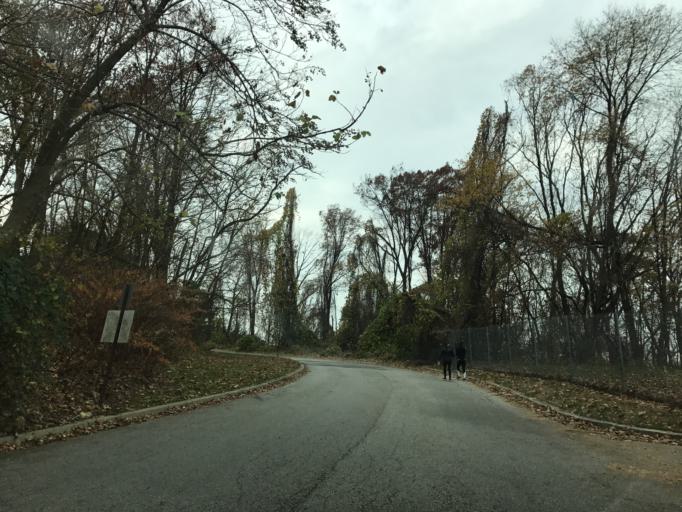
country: US
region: Maryland
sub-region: Baltimore County
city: Hampton
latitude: 39.3995
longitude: -76.5711
